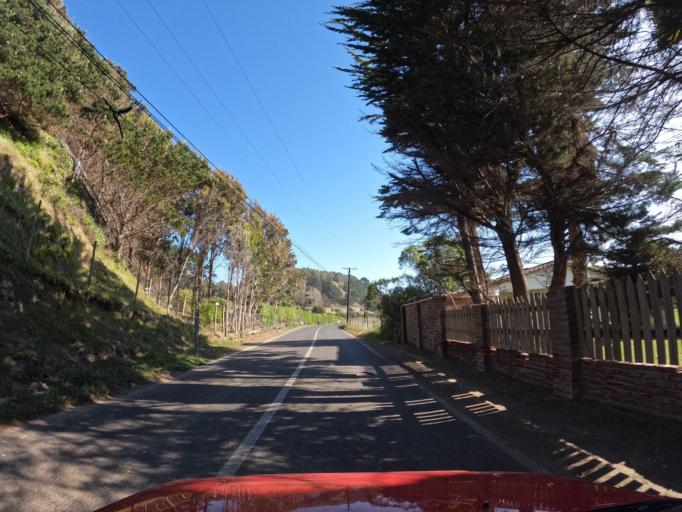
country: CL
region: Maule
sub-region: Provincia de Talca
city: Constitucion
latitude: -34.8669
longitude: -72.1486
